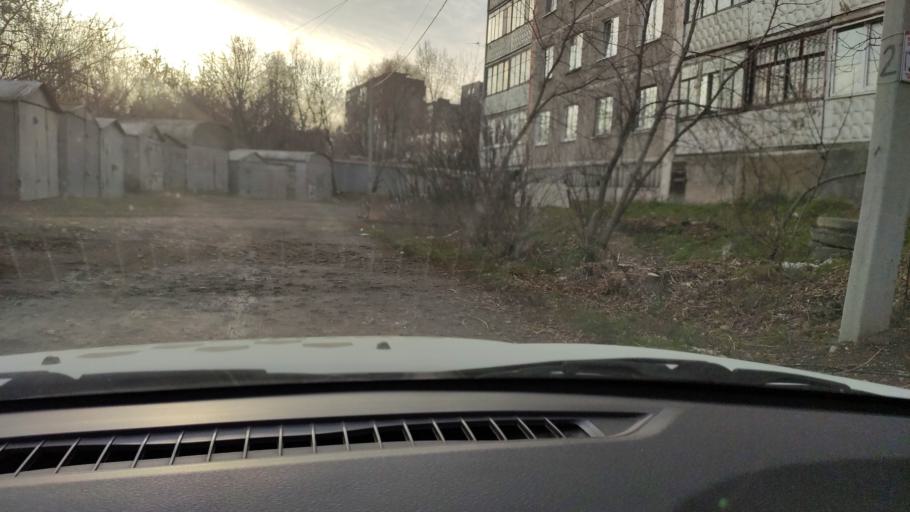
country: RU
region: Perm
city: Perm
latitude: 58.0238
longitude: 56.3063
